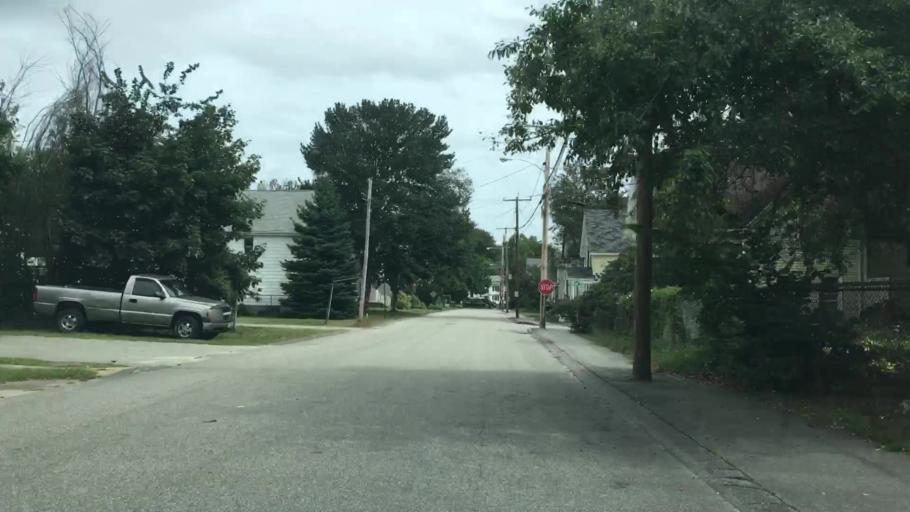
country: US
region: Maine
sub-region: Cumberland County
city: Westbrook
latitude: 43.6725
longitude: -70.3645
